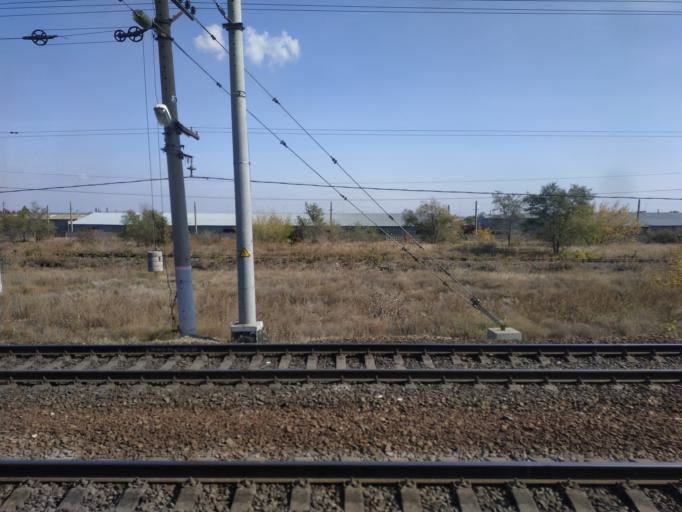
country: RU
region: Volgograd
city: Gumrak
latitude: 48.7895
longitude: 44.3686
